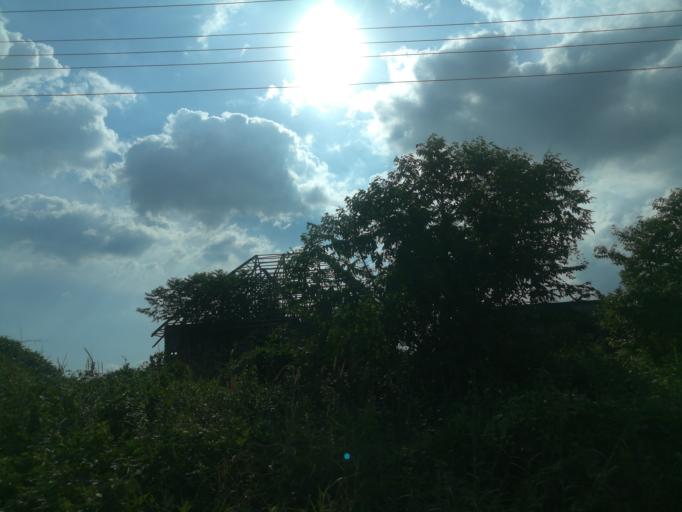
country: NG
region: Oyo
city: Ibadan
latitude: 7.4144
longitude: 3.8350
